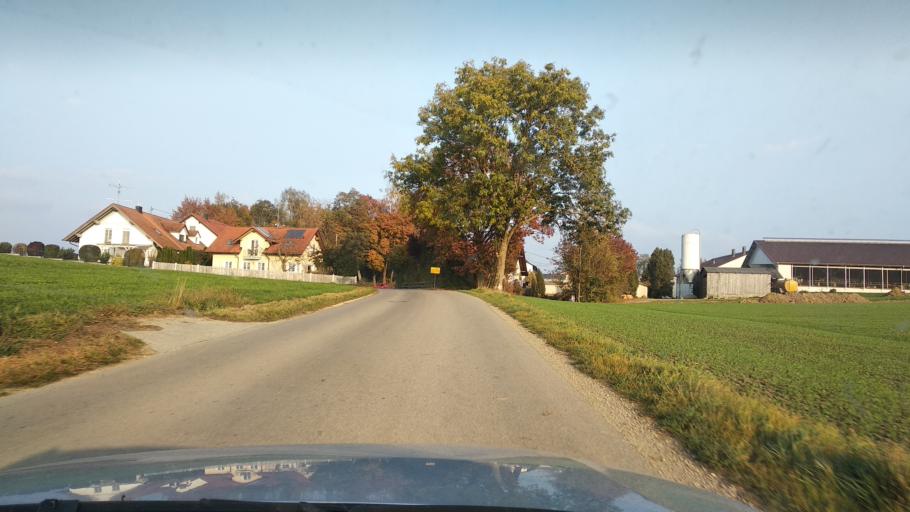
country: DE
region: Bavaria
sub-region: Upper Bavaria
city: Worth
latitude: 48.2389
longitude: 11.9011
